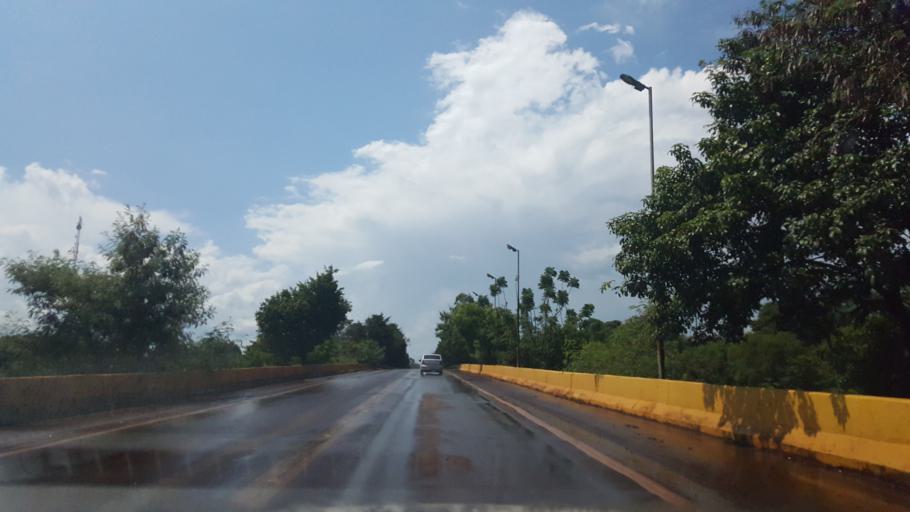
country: AR
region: Misiones
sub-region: Departamento de Eldorado
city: Eldorado
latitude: -26.4036
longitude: -54.6350
